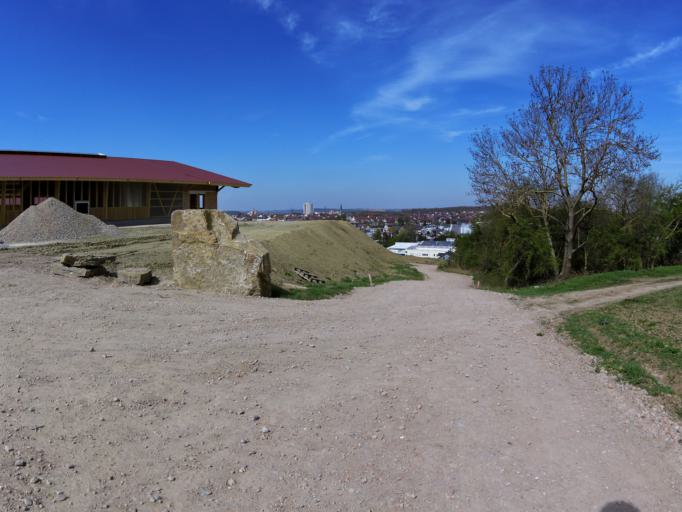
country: DE
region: Bavaria
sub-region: Regierungsbezirk Unterfranken
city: Rottendorf
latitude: 49.7881
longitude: 10.0395
